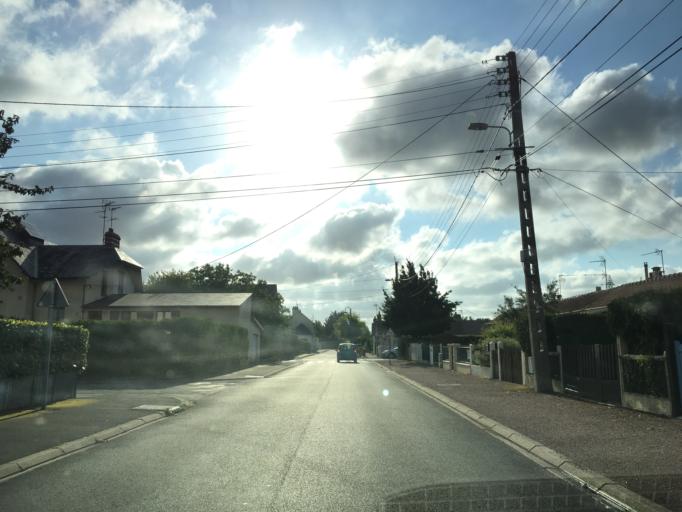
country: FR
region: Lower Normandy
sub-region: Departement du Calvados
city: Dives-sur-Mer
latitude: 49.2835
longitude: -0.1055
